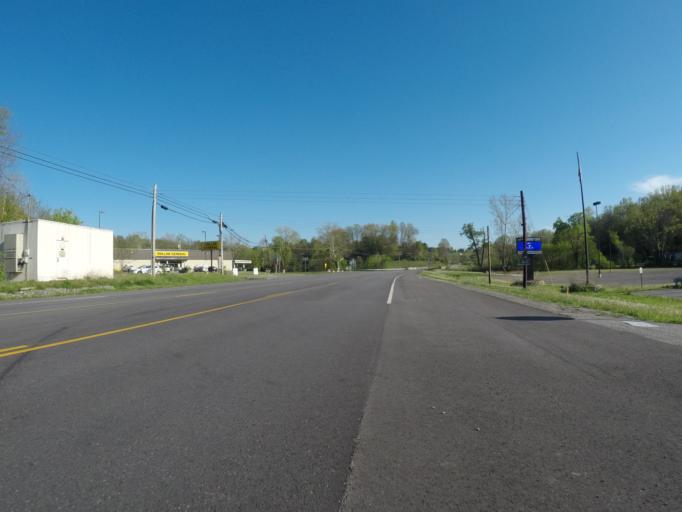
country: US
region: Kentucky
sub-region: Boyd County
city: Meads
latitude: 38.3579
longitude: -82.6974
